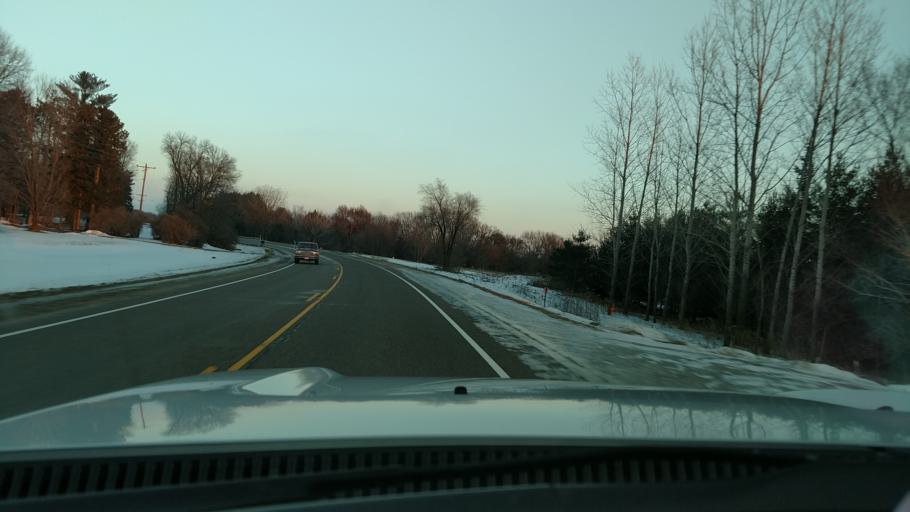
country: US
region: Wisconsin
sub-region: Pierce County
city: River Falls
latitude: 44.8983
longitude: -92.5889
